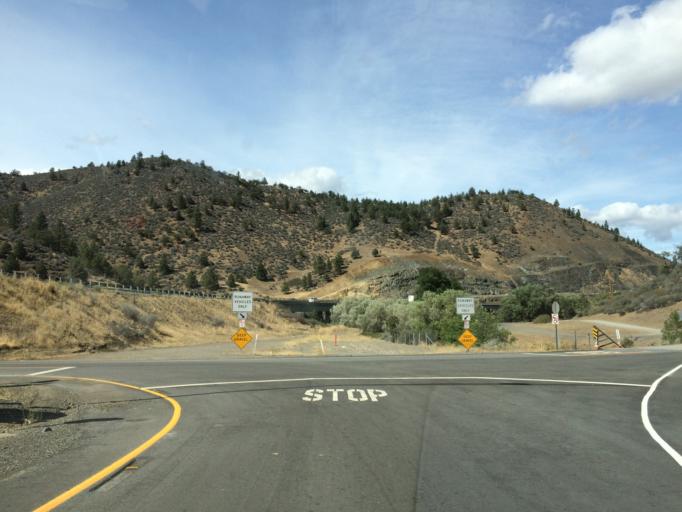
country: US
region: California
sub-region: Siskiyou County
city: Montague
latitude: 41.8546
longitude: -122.5712
